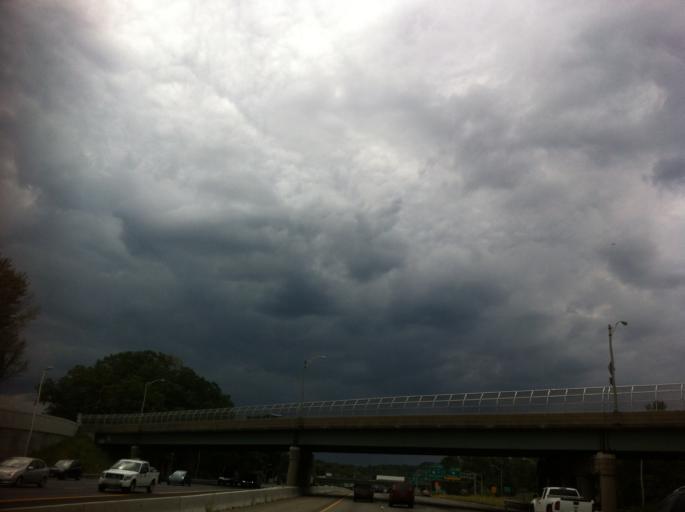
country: US
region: New Jersey
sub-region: Morris County
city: Parsippany
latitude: 40.8620
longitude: -74.4046
